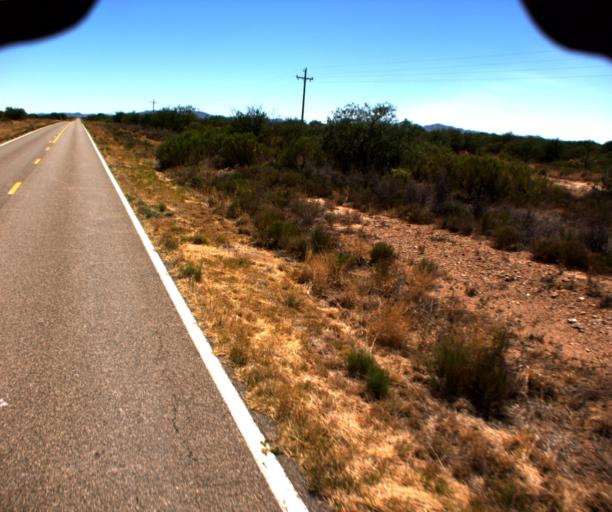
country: US
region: Arizona
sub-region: Pima County
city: Arivaca Junction
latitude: 31.6356
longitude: -111.5050
